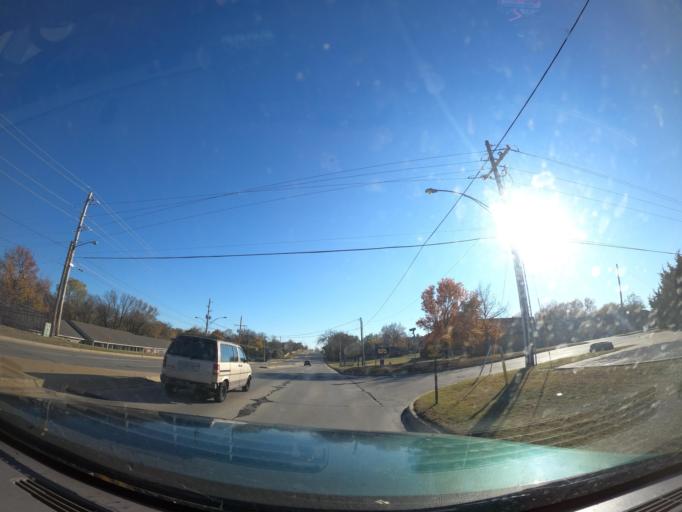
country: US
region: Oklahoma
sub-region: Tulsa County
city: Broken Arrow
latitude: 36.0828
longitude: -95.8866
